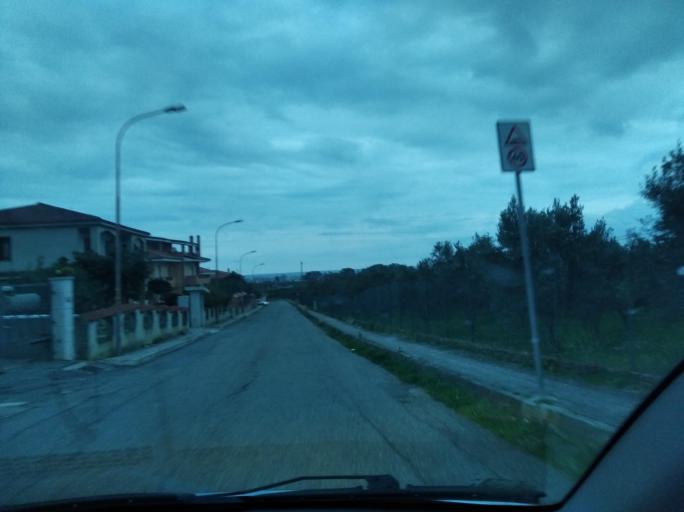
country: IT
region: Calabria
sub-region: Provincia di Catanzaro
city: Montepaone Lido
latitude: 38.7148
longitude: 16.5239
